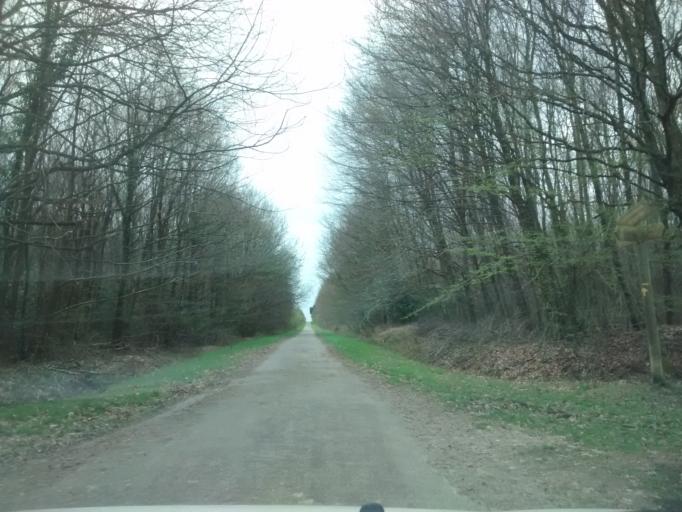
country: FR
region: Brittany
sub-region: Departement d'Ille-et-Vilaine
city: Fouillard
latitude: 48.1693
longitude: -1.5465
